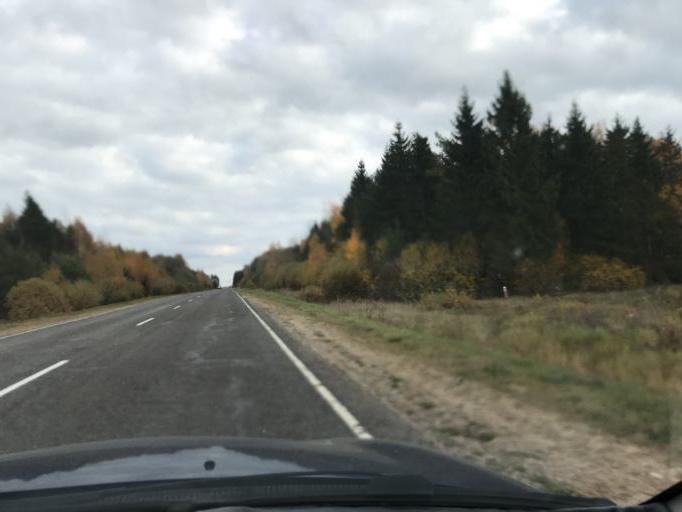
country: BY
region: Grodnenskaya
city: Lida
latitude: 53.7435
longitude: 25.3313
